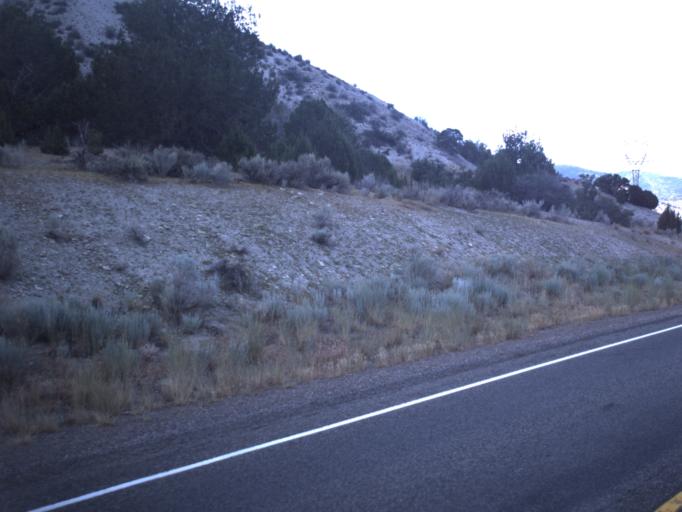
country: US
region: Utah
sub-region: Juab County
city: Nephi
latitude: 39.7179
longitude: -111.7536
